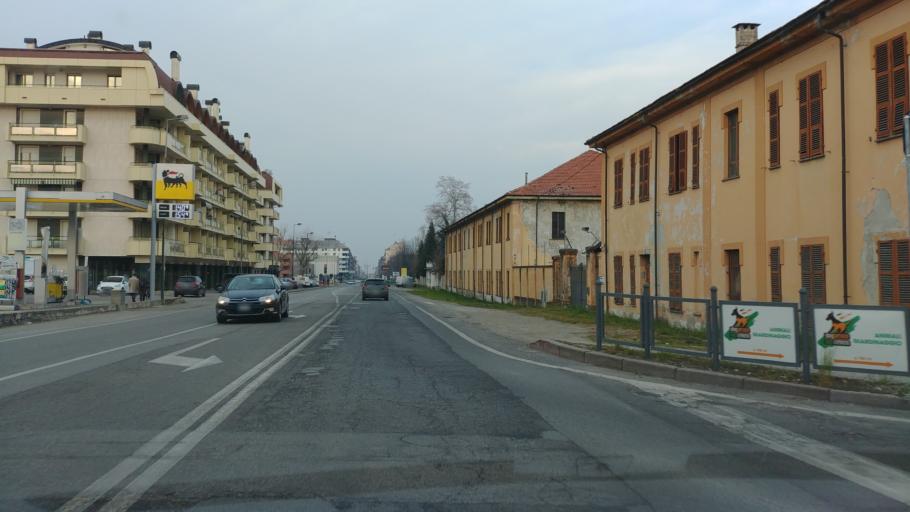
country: IT
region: Piedmont
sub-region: Provincia di Cuneo
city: Cuneo
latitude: 44.3744
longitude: 7.5323
